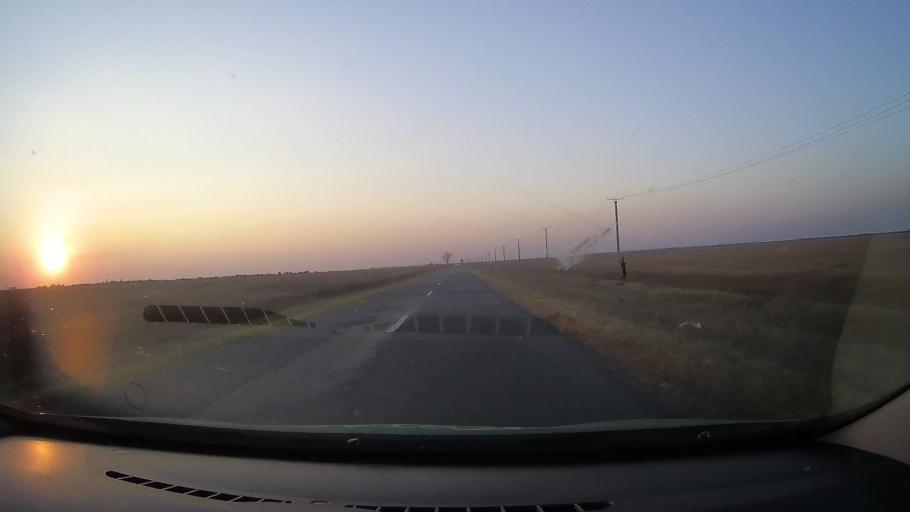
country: RO
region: Arad
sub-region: Comuna Zarand
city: Zarand
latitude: 46.4140
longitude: 21.6266
